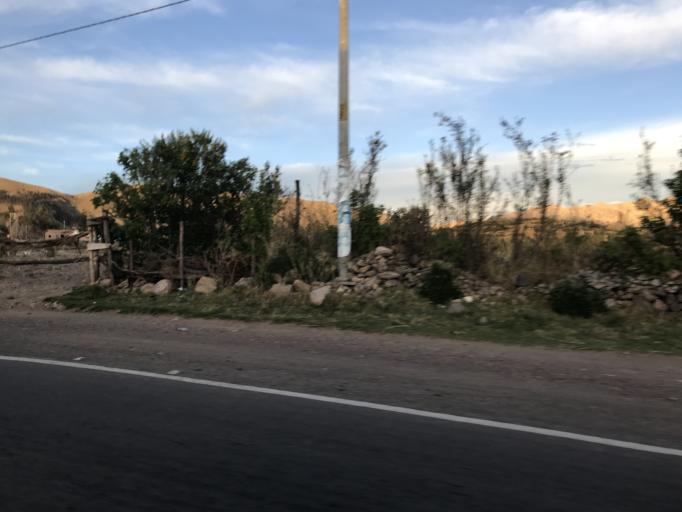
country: PE
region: Cusco
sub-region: Provincia de Cusco
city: Cusco
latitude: -13.4935
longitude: -71.9673
